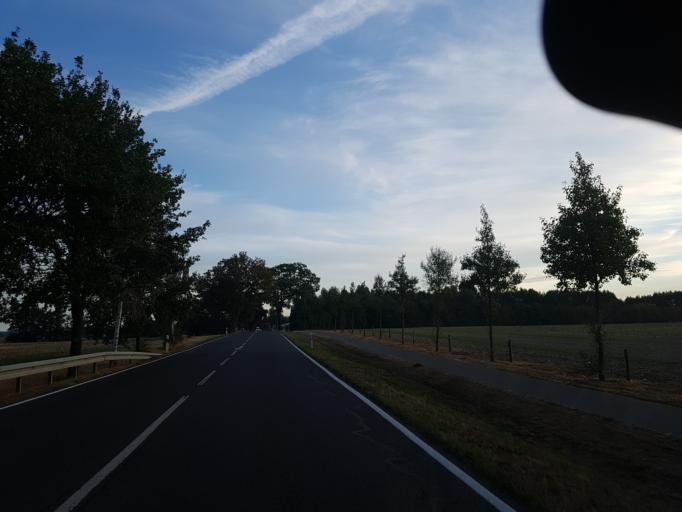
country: DE
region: Brandenburg
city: Sonnewalde
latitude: 51.6735
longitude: 13.6419
